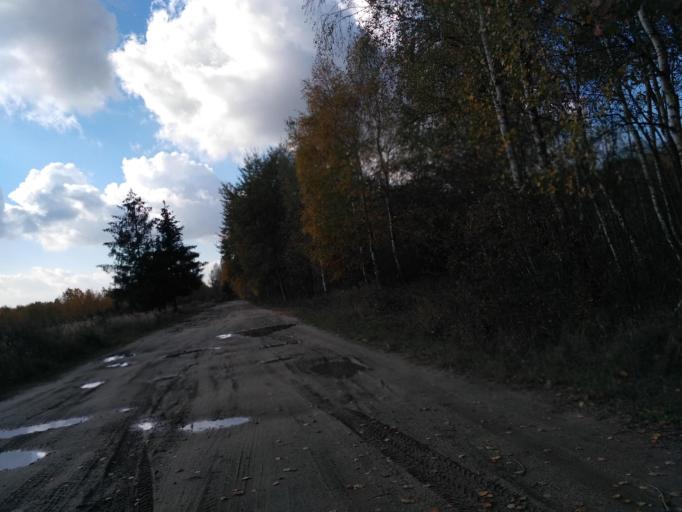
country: PL
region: Subcarpathian Voivodeship
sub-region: Powiat rzeszowski
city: Glogow Malopolski
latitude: 50.1319
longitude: 21.9197
